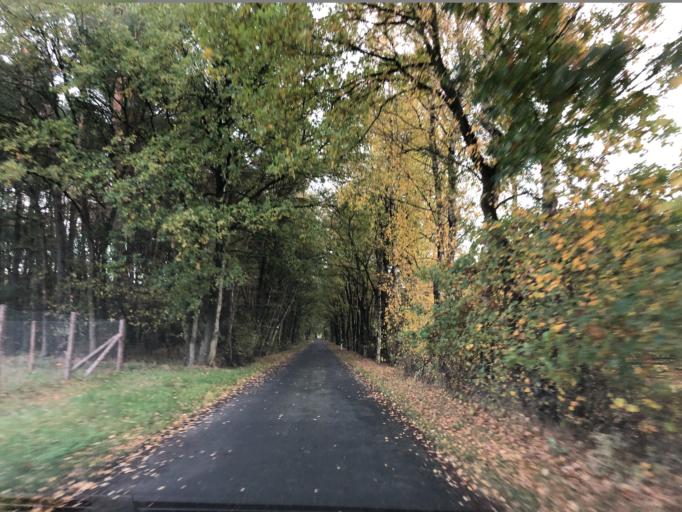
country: DE
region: Lower Saxony
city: Lehe
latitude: 53.0247
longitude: 7.3413
